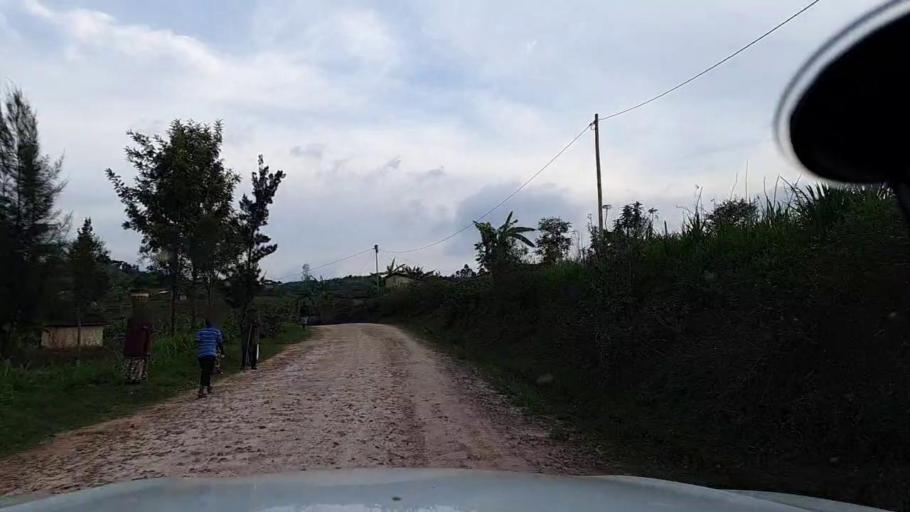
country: RW
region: Southern Province
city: Gitarama
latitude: -2.2086
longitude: 29.6061
